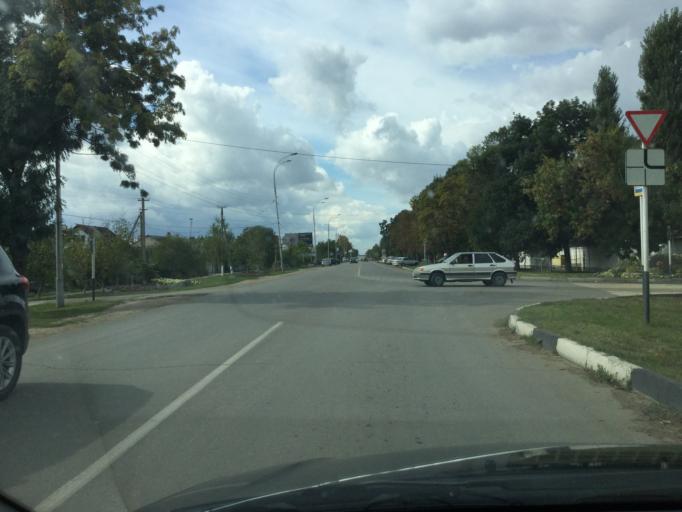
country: RU
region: Krasnodarskiy
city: Slavyansk-na-Kubani
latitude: 45.2524
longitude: 38.1080
